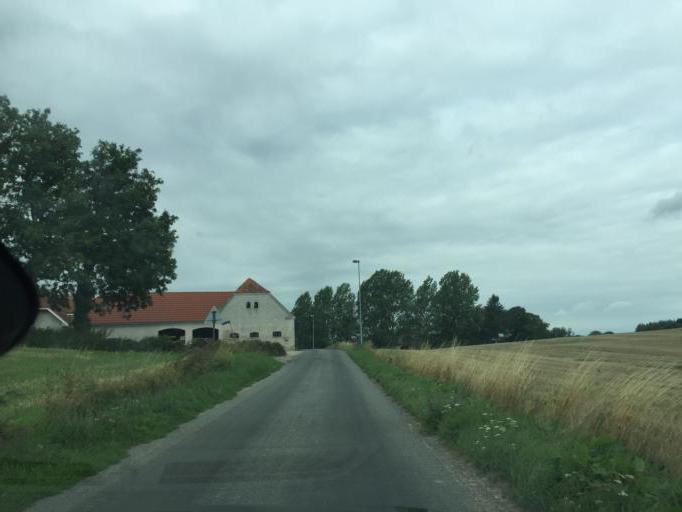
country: DK
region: South Denmark
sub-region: Assens Kommune
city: Vissenbjerg
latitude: 55.3668
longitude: 10.1258
